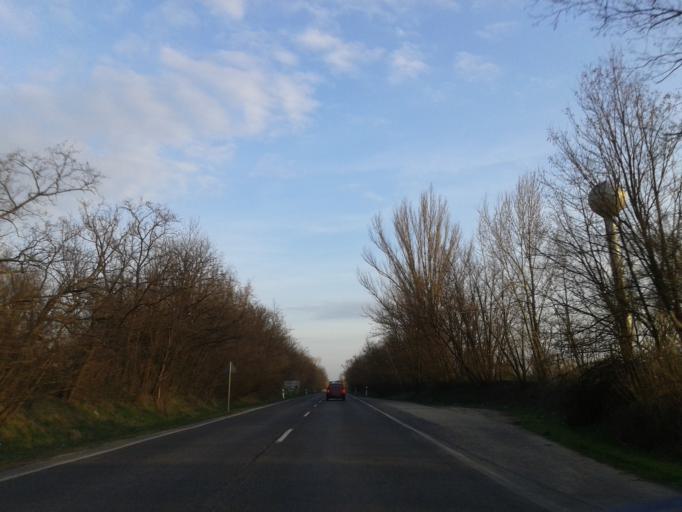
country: HU
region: Komarom-Esztergom
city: Szomod
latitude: 47.6933
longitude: 18.3085
